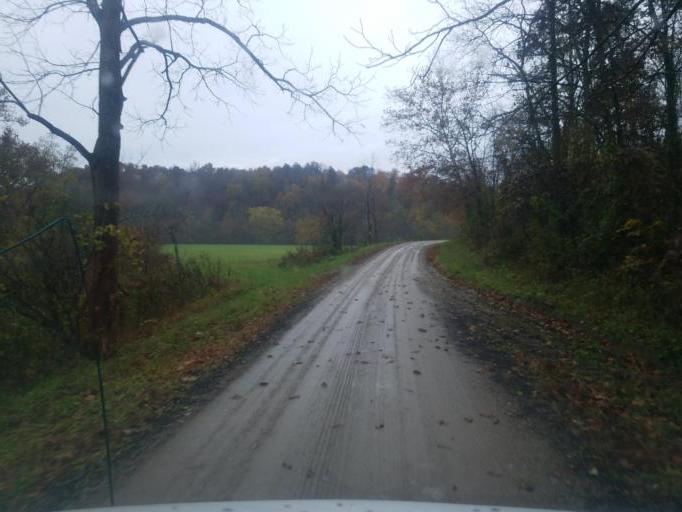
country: US
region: Ohio
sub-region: Washington County
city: Beverly
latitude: 39.4586
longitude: -81.7695
